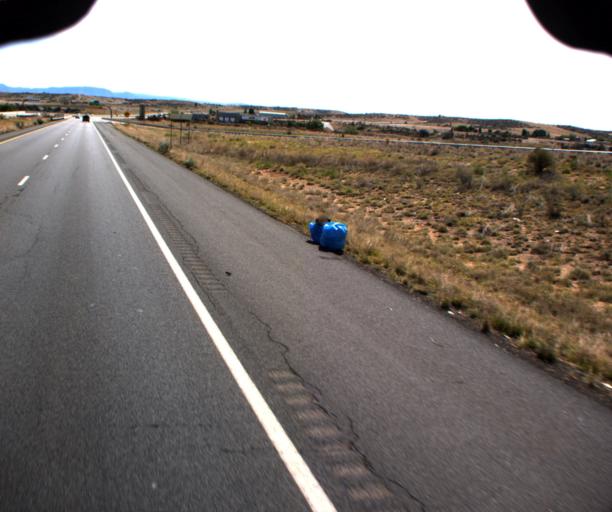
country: US
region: Arizona
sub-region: Yavapai County
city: Prescott Valley
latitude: 34.6354
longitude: -112.4156
